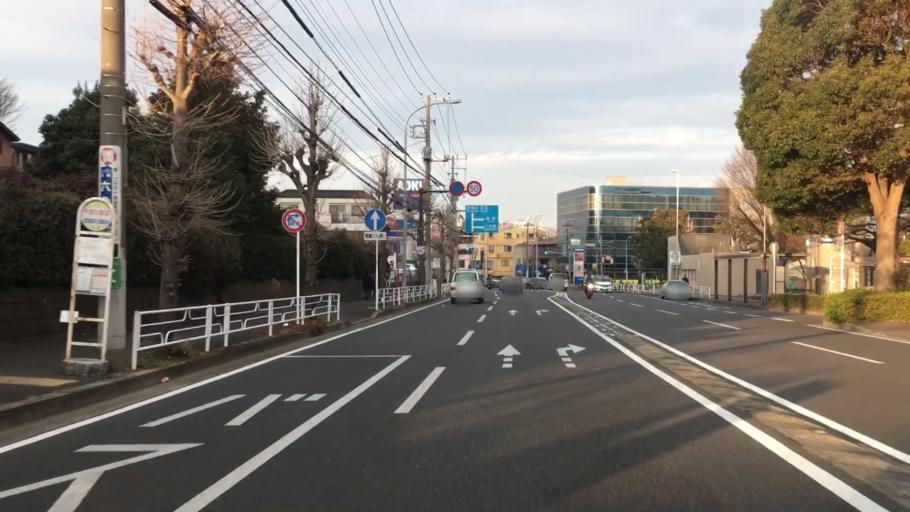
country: JP
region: Kanagawa
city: Yokohama
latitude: 35.4897
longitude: 139.6061
